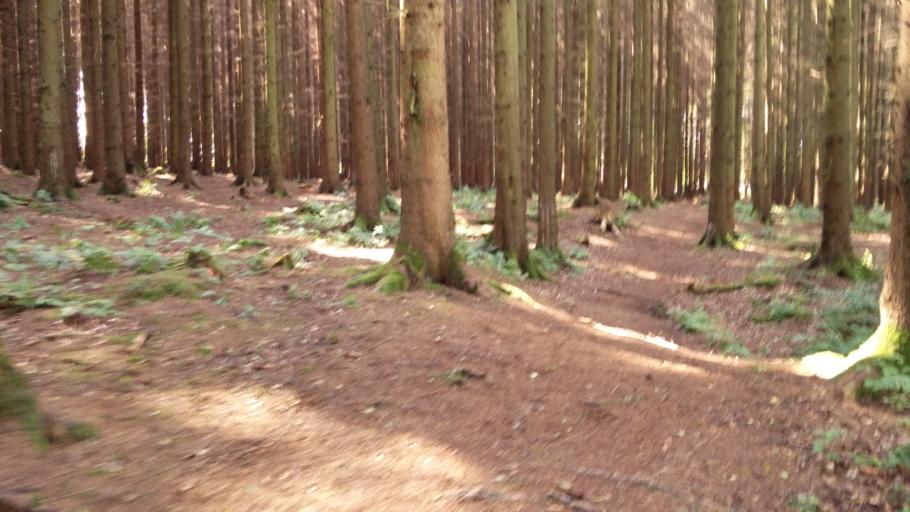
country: DE
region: Hesse
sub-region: Regierungsbezirk Kassel
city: Immenhausen
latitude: 51.4376
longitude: 9.5138
